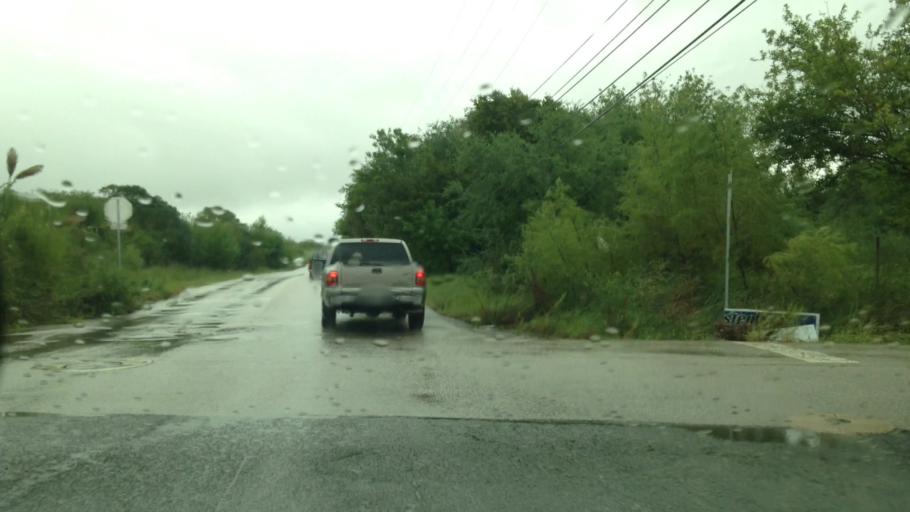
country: US
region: Texas
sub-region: Bexar County
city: Windcrest
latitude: 29.5554
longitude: -98.3798
